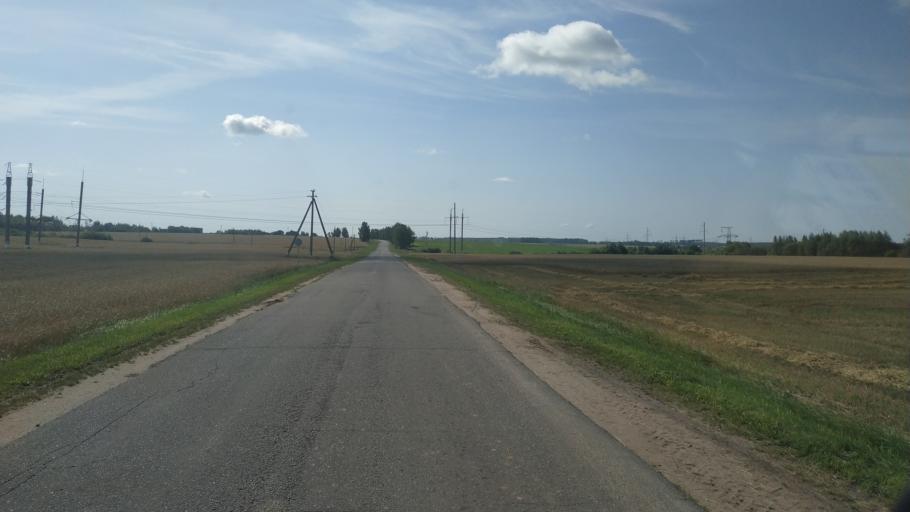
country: BY
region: Mogilev
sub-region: Mahilyowski Rayon
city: Veyno
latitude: 53.7914
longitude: 30.4310
